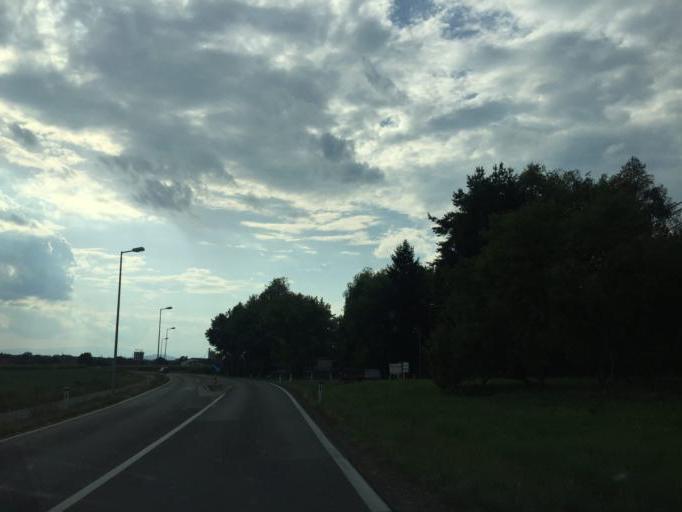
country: AT
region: Styria
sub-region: Politischer Bezirk Suedoststeiermark
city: Weinburg am Sassbach
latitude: 46.7571
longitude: 15.6824
